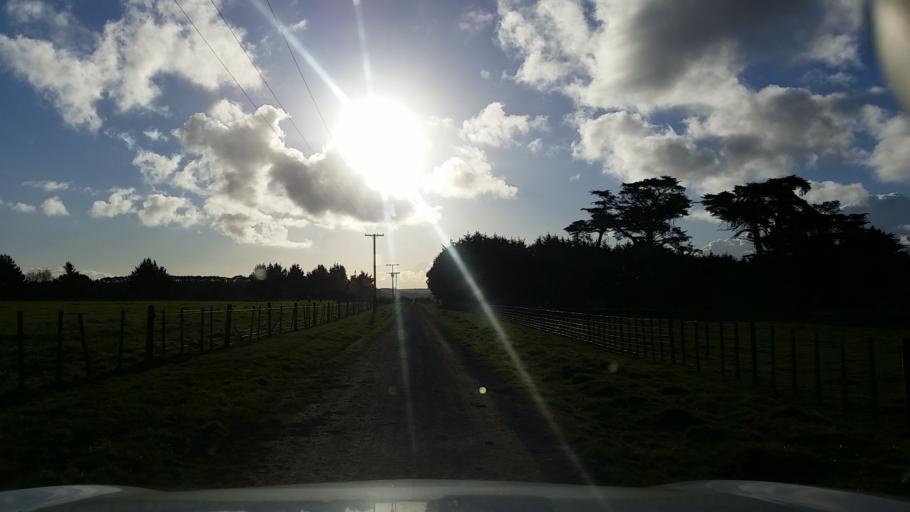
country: NZ
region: Taranaki
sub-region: South Taranaki District
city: Patea
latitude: -39.6156
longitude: 174.4940
